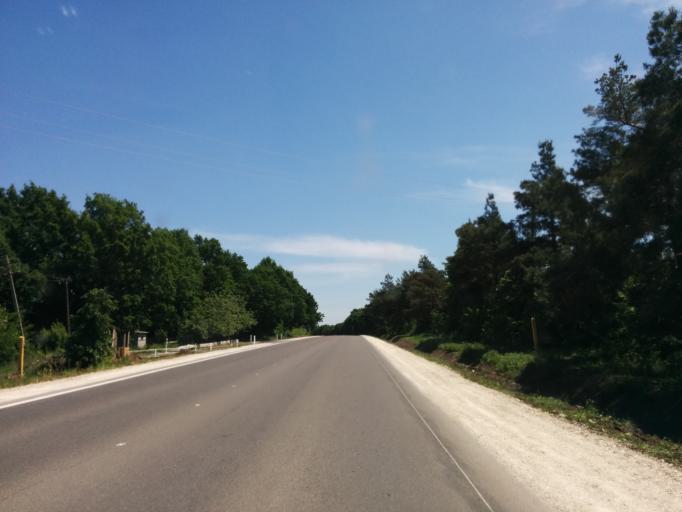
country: MD
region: Raionul Soroca
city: Soroca
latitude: 48.1649
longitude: 28.2393
